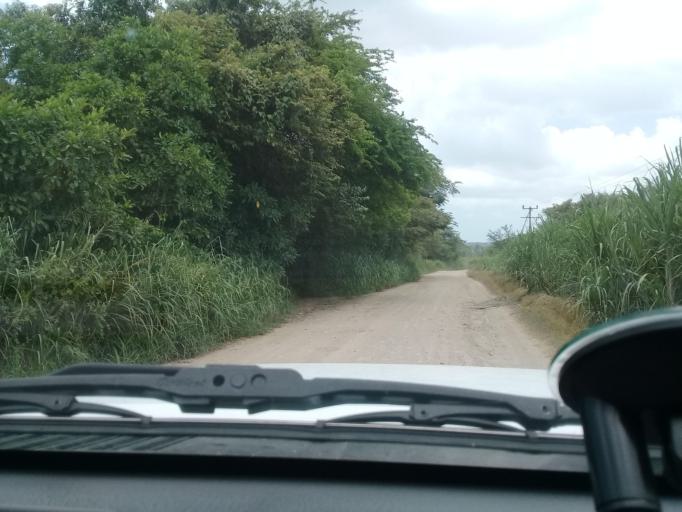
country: MX
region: Veracruz
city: Panuco
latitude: 22.1300
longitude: -98.0641
